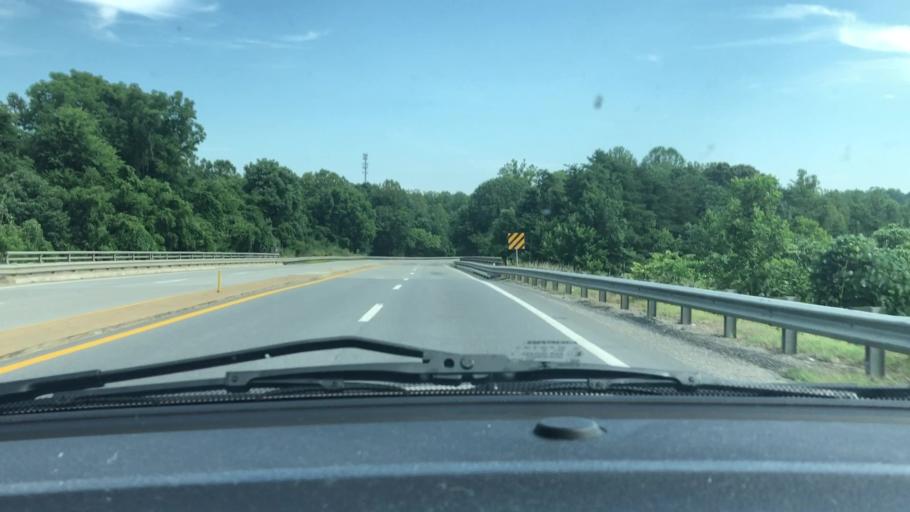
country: US
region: Virginia
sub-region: Henry County
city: Chatmoss
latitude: 36.5842
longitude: -79.8632
